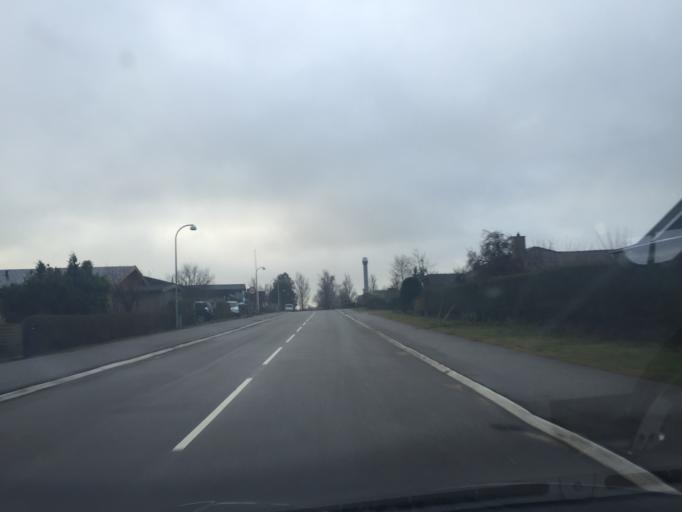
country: DK
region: Capital Region
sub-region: Hoje-Taastrup Kommune
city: Flong
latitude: 55.6813
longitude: 12.2388
